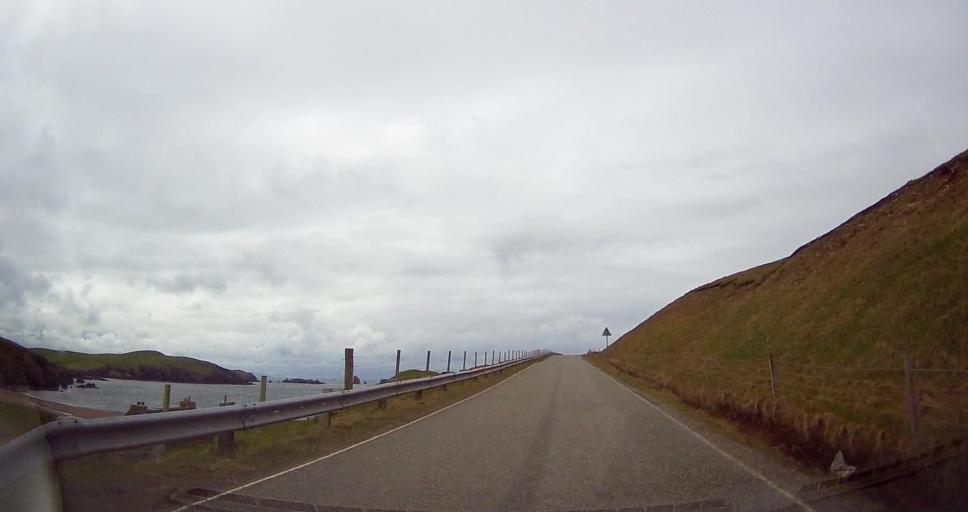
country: GB
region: Scotland
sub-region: Shetland Islands
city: Lerwick
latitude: 60.4874
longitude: -1.4964
